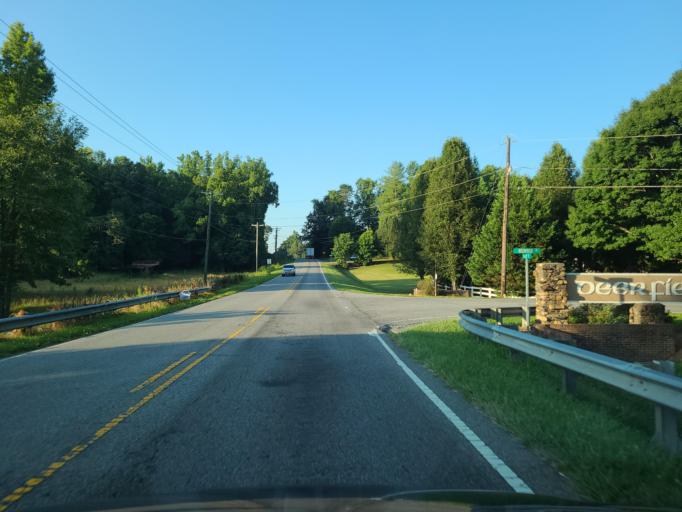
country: US
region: North Carolina
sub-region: Catawba County
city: Mountain View
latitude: 35.6531
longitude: -81.3808
